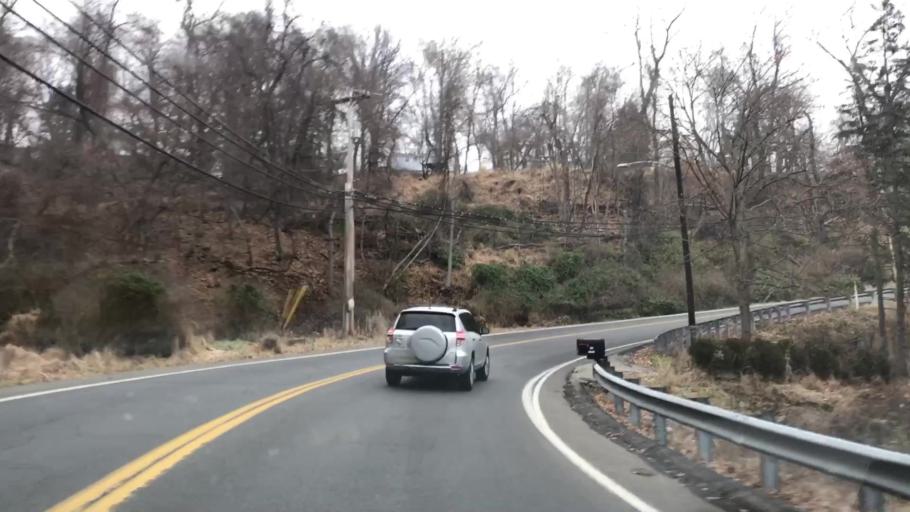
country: US
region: Pennsylvania
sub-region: Allegheny County
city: Leetsdale
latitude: 40.5688
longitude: -80.2048
